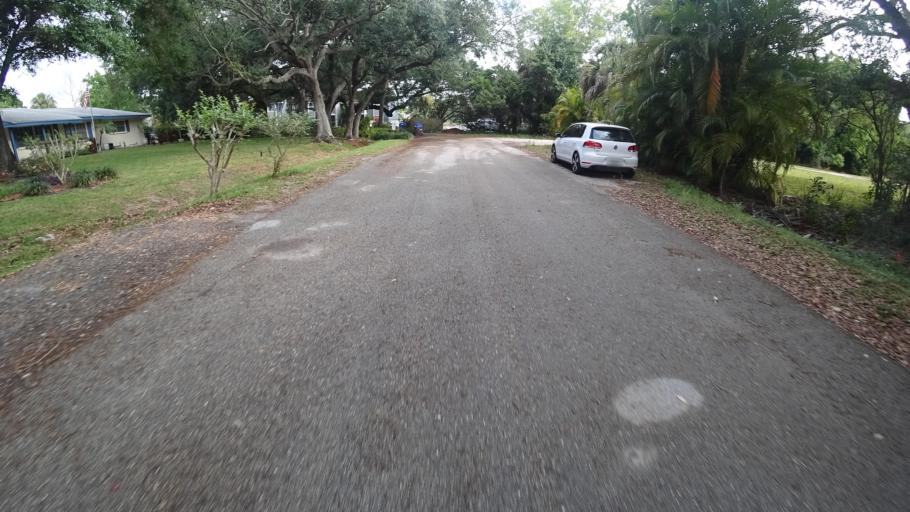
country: US
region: Florida
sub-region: Manatee County
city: Bayshore Gardens
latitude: 27.4437
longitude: -82.5901
